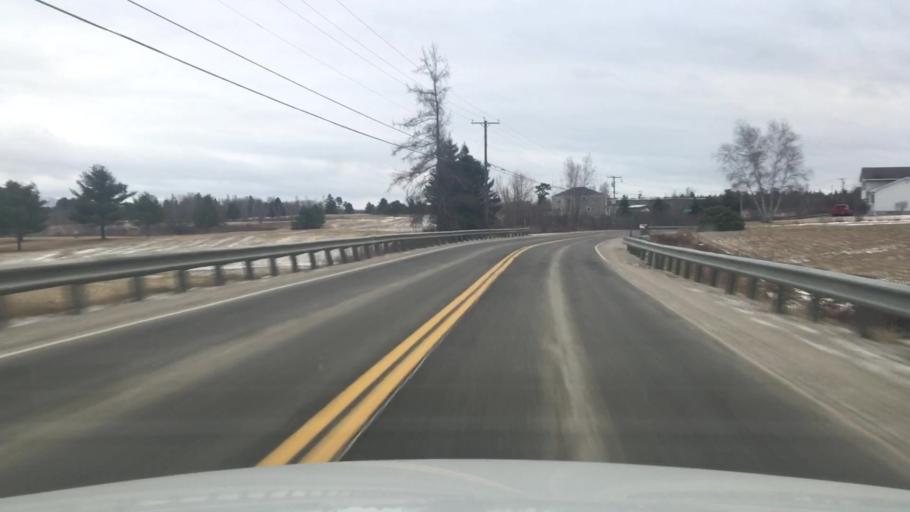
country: US
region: Maine
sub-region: Hancock County
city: Trenton
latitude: 44.4919
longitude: -68.3632
